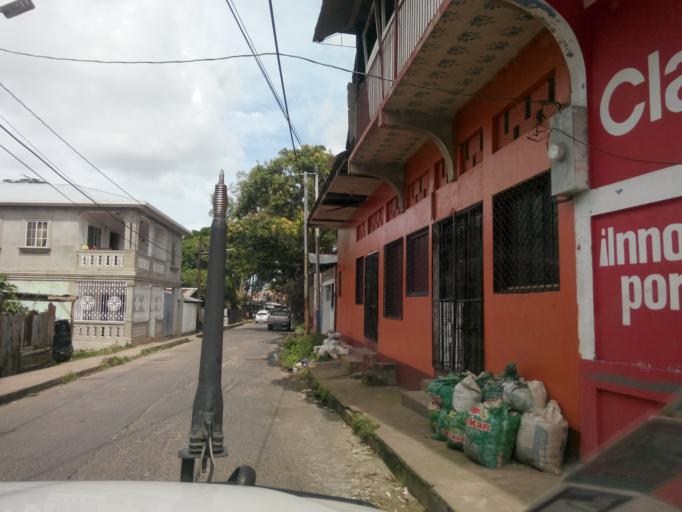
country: NI
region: Atlantico Sur
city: Bluefields
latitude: 12.0130
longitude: -83.7717
